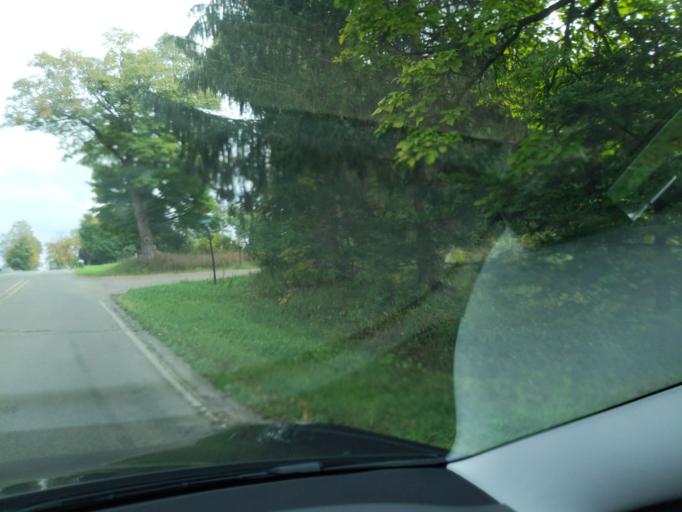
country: US
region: Michigan
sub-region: Ingham County
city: Leslie
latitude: 42.4112
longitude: -84.3946
